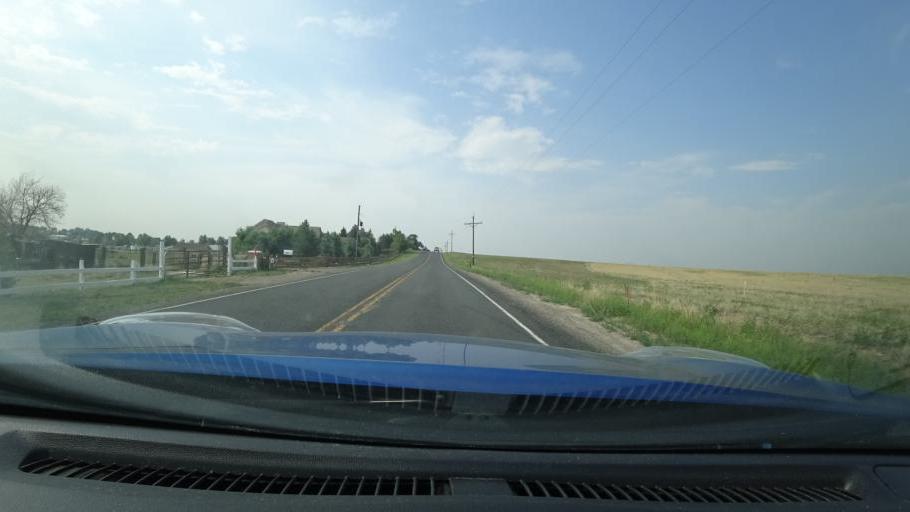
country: US
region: Colorado
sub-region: Adams County
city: Aurora
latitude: 39.7261
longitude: -104.7349
